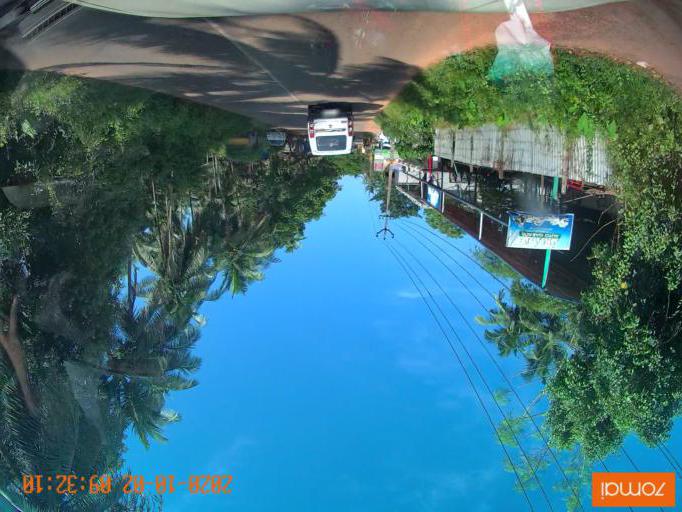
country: IN
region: Kerala
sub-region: Kozhikode
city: Nadapuram
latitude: 11.6265
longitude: 75.7571
